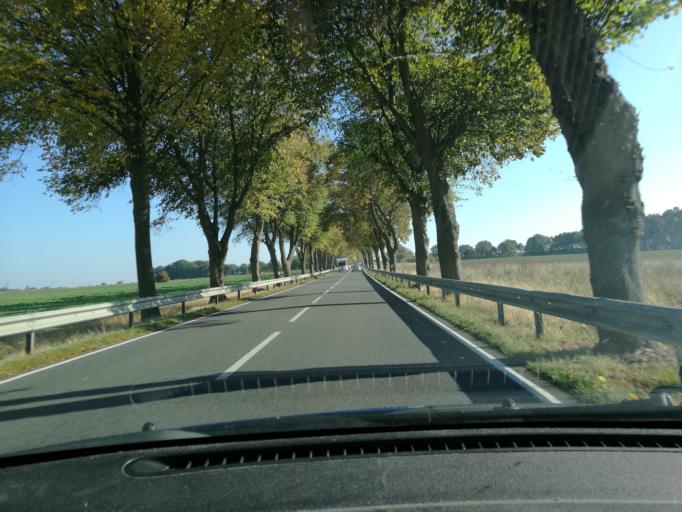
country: DE
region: Lower Saxony
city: Nahrendorf
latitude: 53.1647
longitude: 10.7941
